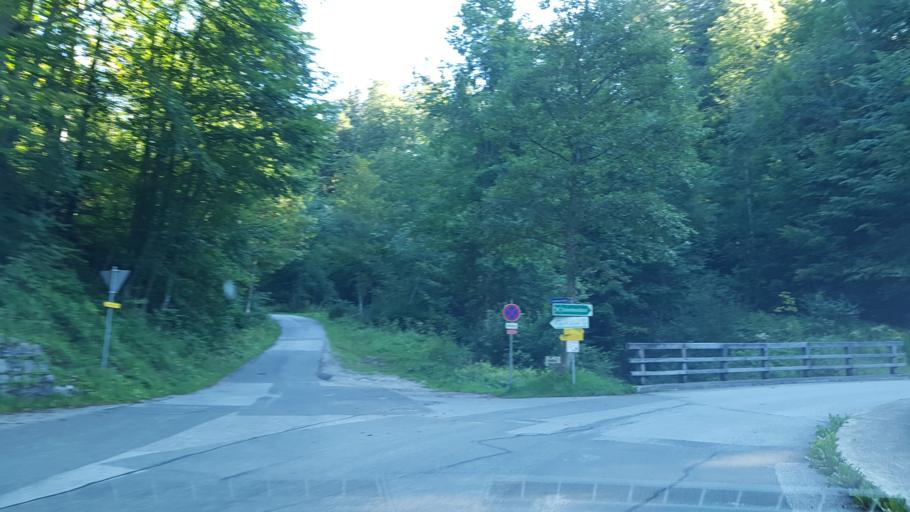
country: AT
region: Salzburg
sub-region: Politischer Bezirk Hallein
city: Krispl
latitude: 47.7042
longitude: 13.2210
